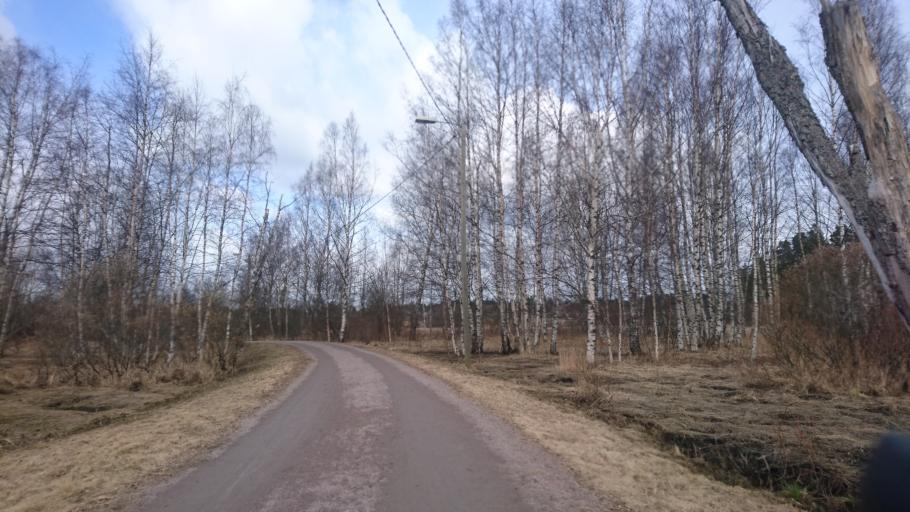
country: FI
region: Uusimaa
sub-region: Helsinki
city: Espoo
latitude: 60.2158
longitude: 24.6772
